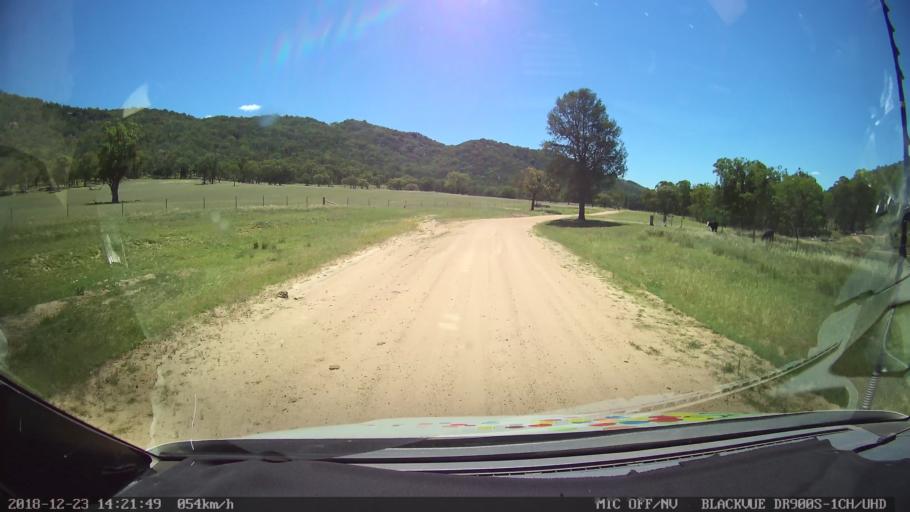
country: AU
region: New South Wales
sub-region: Tamworth Municipality
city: Manilla
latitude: -30.6448
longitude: 150.9777
